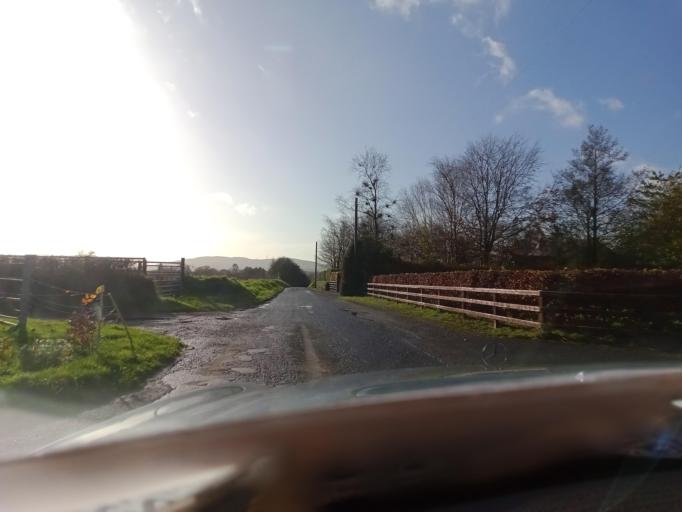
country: IE
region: Munster
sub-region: Waterford
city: Portlaw
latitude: 52.3238
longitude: -7.2920
